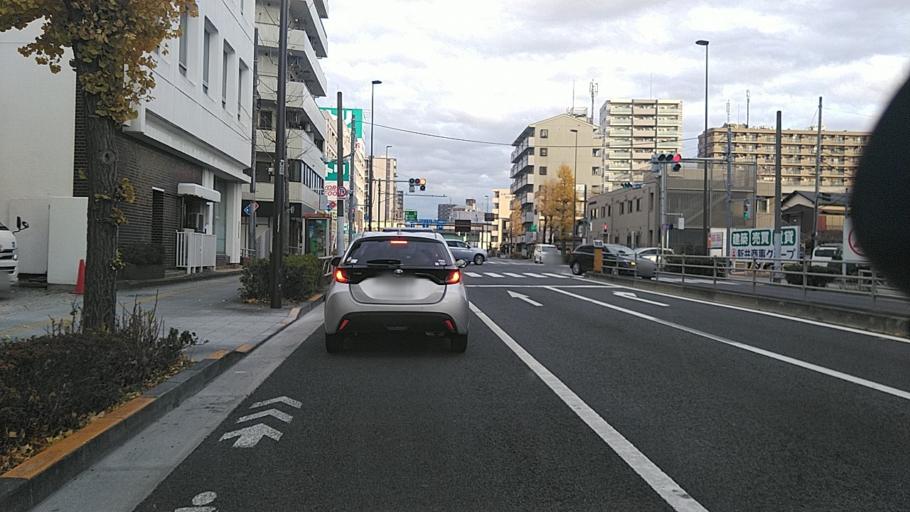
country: JP
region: Saitama
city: Soka
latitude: 35.7767
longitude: 139.8032
